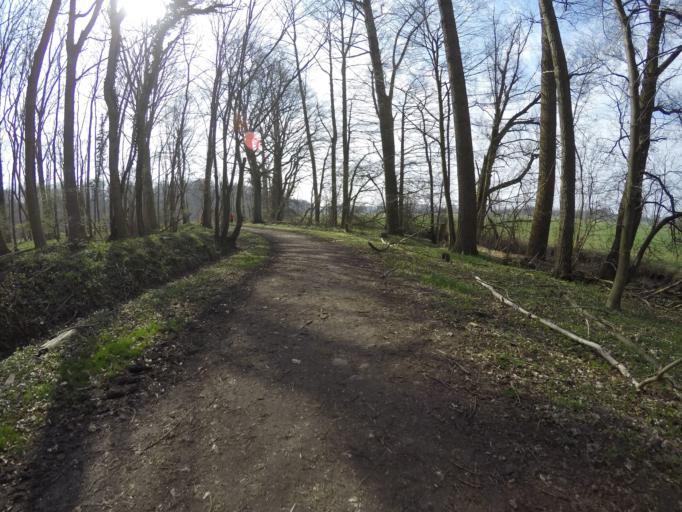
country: DE
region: Schleswig-Holstein
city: Ellerhoop
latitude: 53.7237
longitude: 9.8048
